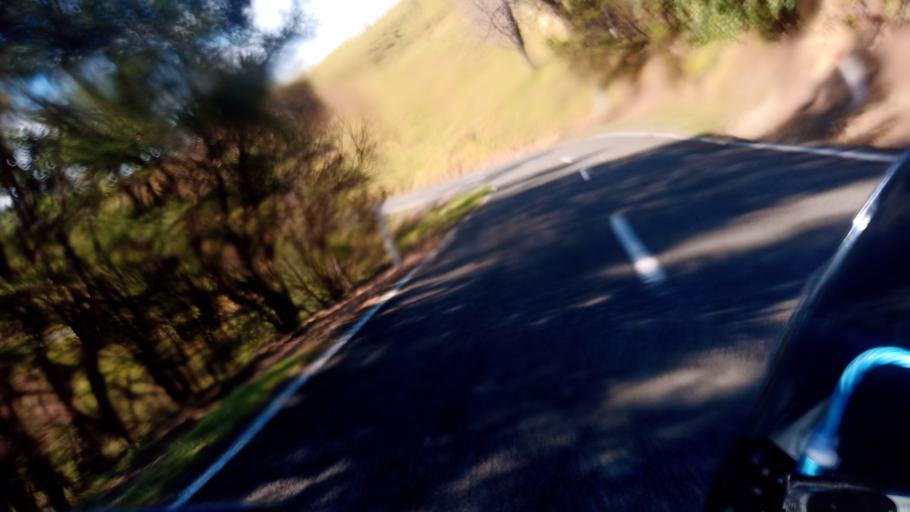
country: NZ
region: Gisborne
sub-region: Gisborne District
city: Gisborne
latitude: -38.2500
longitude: 178.3060
